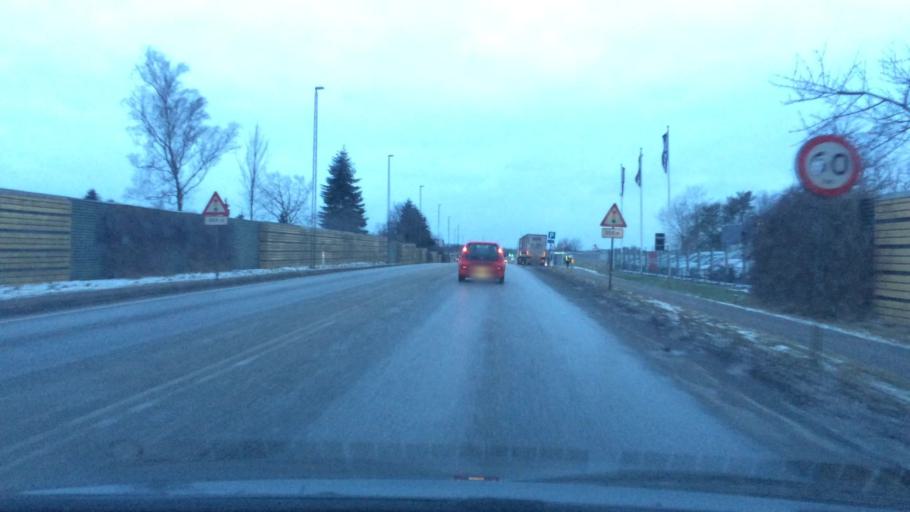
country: DK
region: Central Jutland
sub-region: Horsens Kommune
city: Horsens
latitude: 55.8357
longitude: 9.8104
